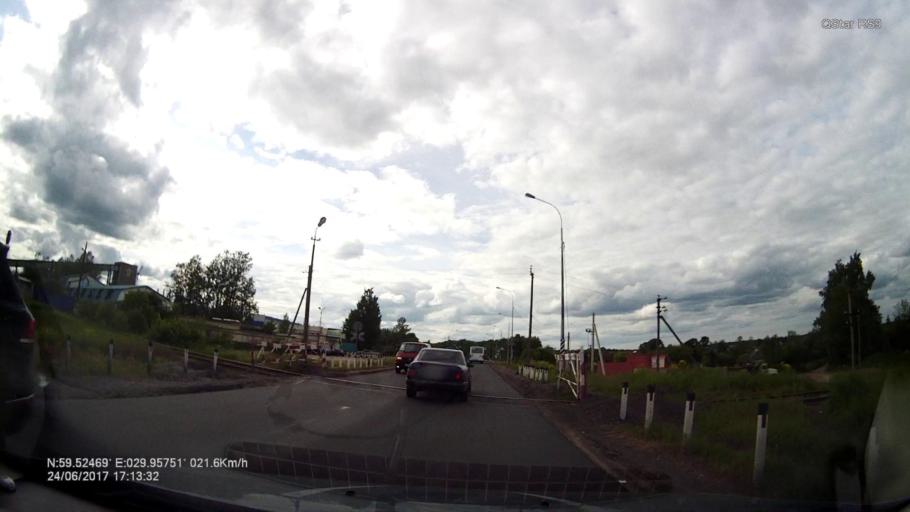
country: RU
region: Leningrad
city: Voyskovitsy
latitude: 59.5247
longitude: 29.9574
